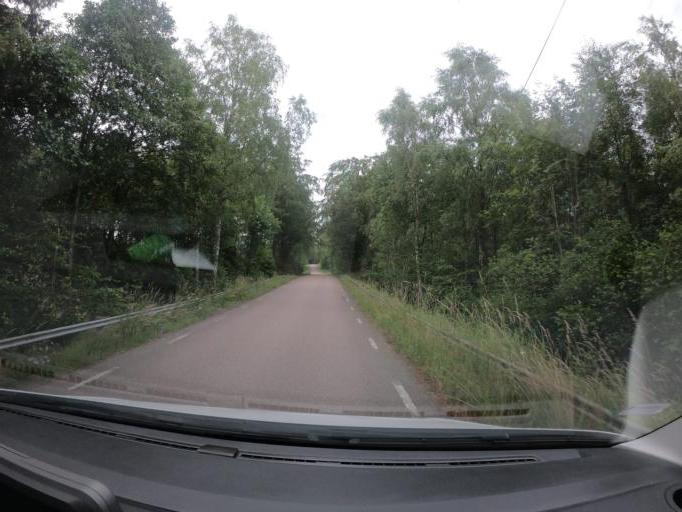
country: SE
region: Skane
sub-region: Orkelljunga Kommun
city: OErkelljunga
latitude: 56.3536
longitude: 13.1231
